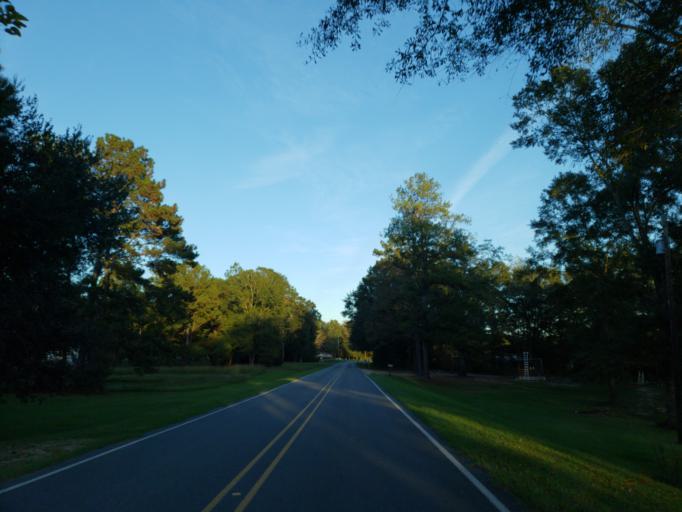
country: US
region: Mississippi
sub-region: Wayne County
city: Belmont
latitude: 31.4411
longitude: -88.5050
